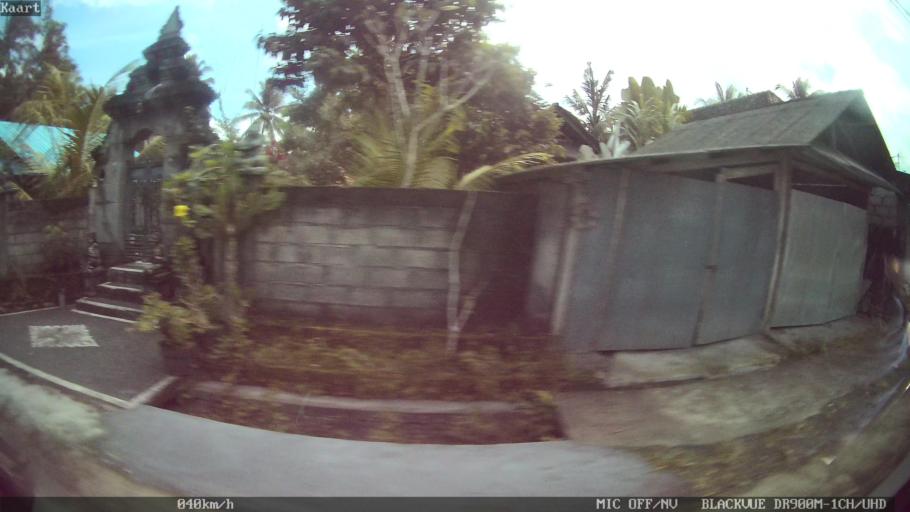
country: ID
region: Bali
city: Banjar Bebalang
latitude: -8.4761
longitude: 115.3419
